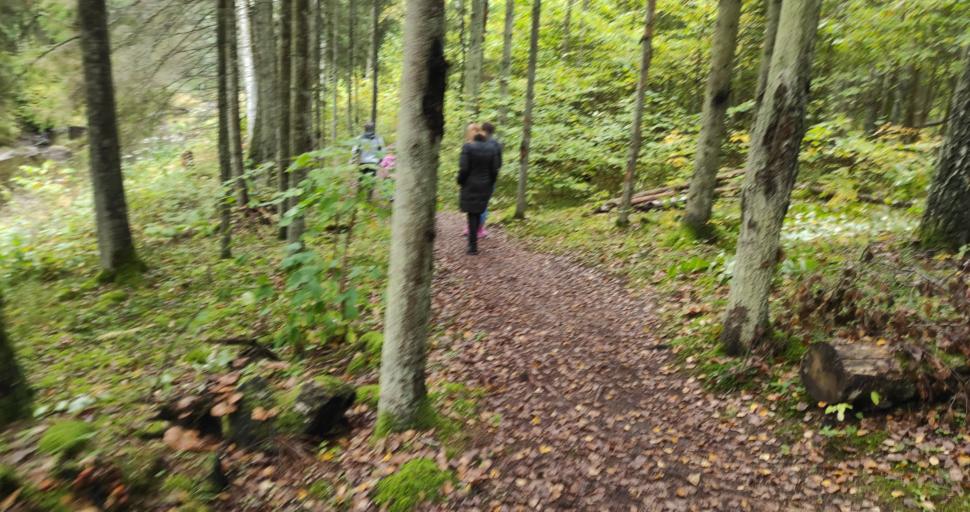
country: LV
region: Jaunpils
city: Jaunpils
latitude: 56.8126
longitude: 22.9496
